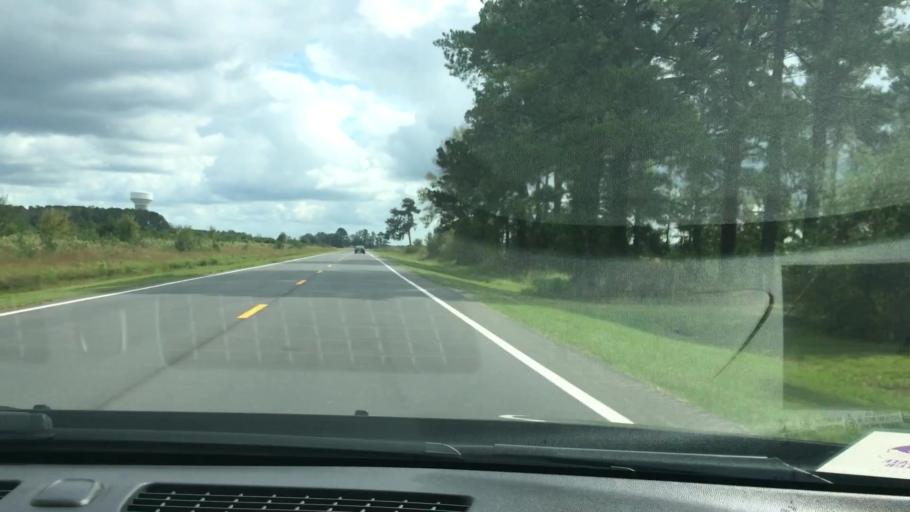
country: US
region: North Carolina
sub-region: Pitt County
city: Farmville
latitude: 35.5543
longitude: -77.5530
